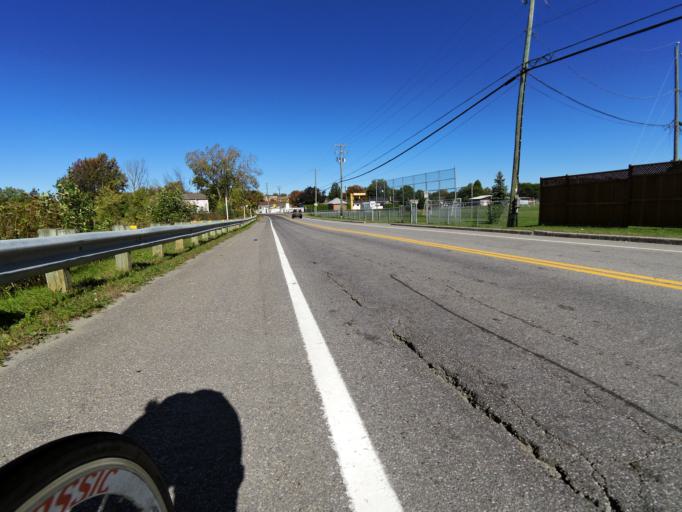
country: CA
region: Ontario
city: Clarence-Rockland
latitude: 45.5410
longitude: -75.4155
